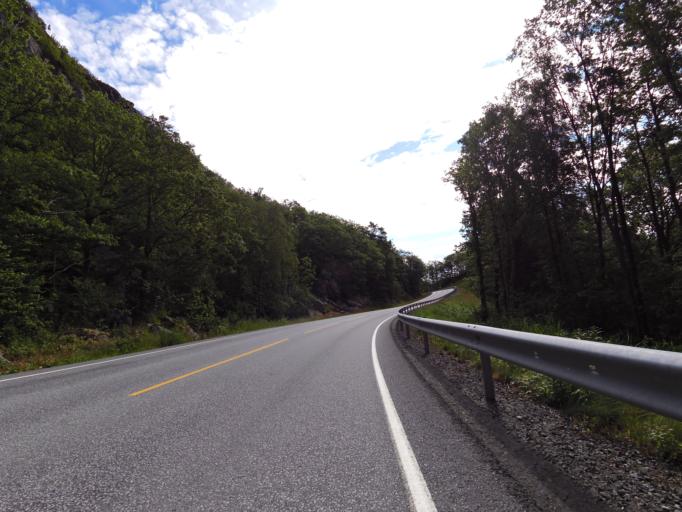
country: NO
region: Vest-Agder
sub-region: Lyngdal
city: Lyngdal
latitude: 58.0494
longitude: 7.1708
